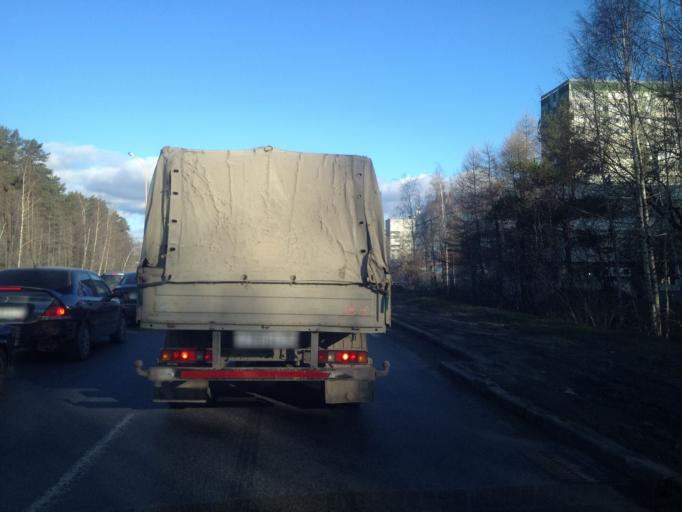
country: RU
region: Sverdlovsk
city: Sovkhoznyy
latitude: 56.7901
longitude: 60.5776
